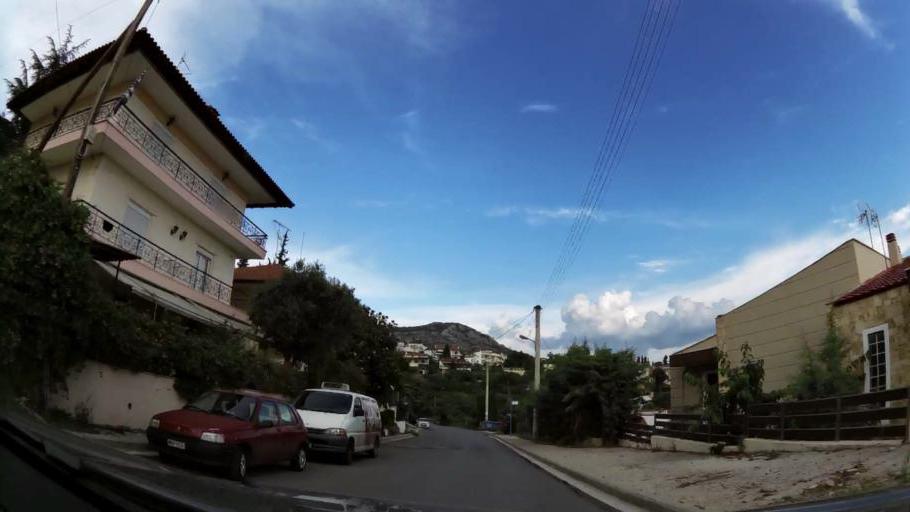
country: GR
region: Central Macedonia
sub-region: Nomos Thessalonikis
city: Pefka
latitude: 40.6591
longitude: 22.9958
